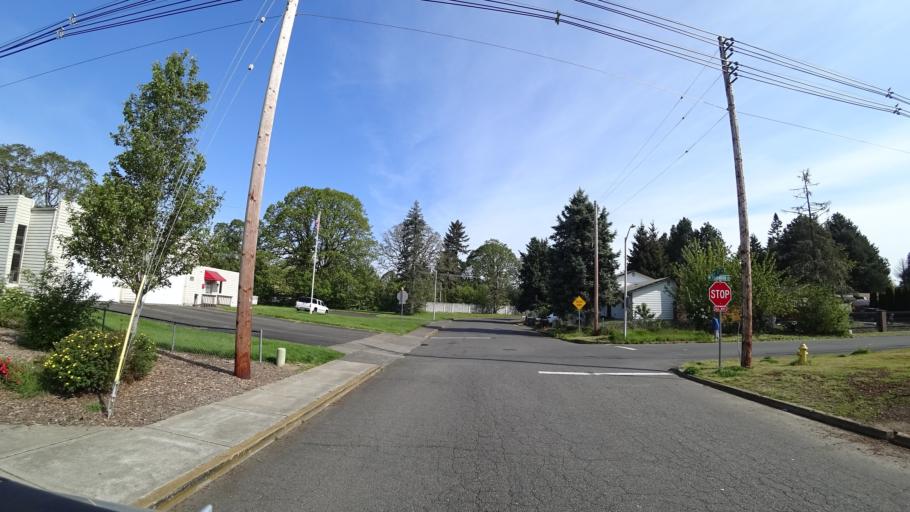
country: US
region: Oregon
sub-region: Washington County
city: Hillsboro
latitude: 45.5237
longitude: -122.9565
